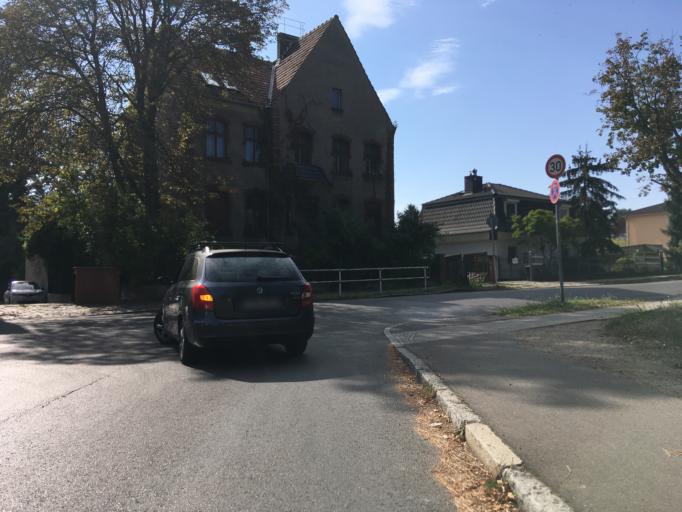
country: DE
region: Berlin
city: Mahlsdorf
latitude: 52.5124
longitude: 13.6199
